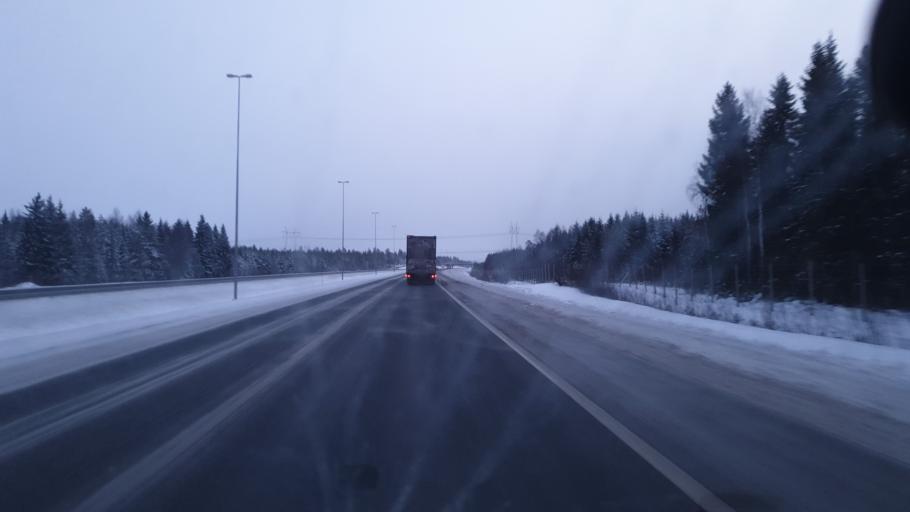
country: FI
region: Lapland
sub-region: Kemi-Tornio
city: Tornio
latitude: 65.8377
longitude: 24.3224
